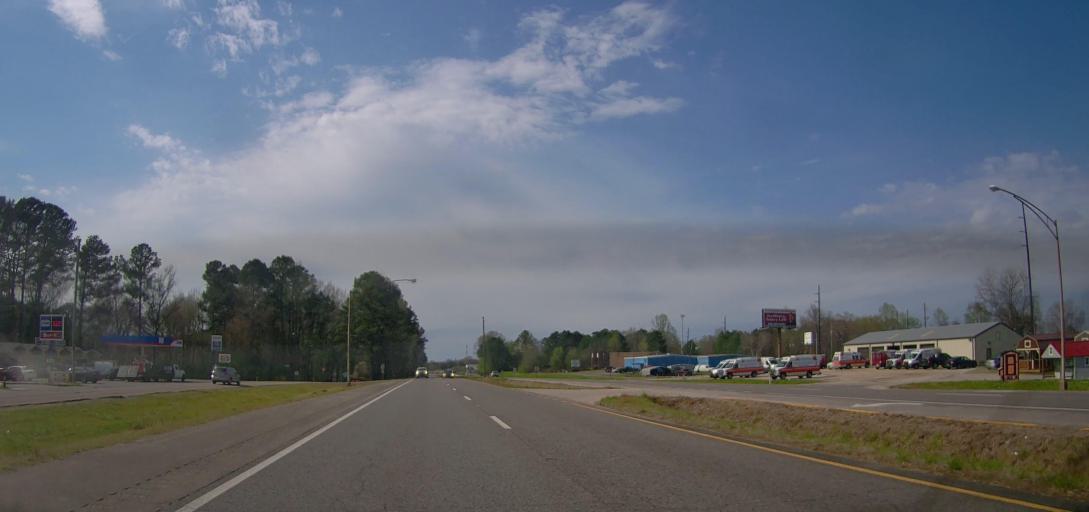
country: US
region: Alabama
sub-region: Jefferson County
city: Adamsville
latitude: 33.5895
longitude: -86.9366
